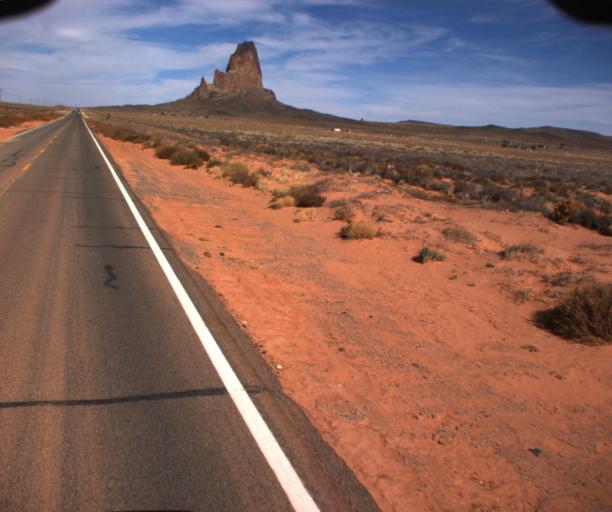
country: US
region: Arizona
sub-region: Navajo County
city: Kayenta
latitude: 36.7947
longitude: -110.2314
